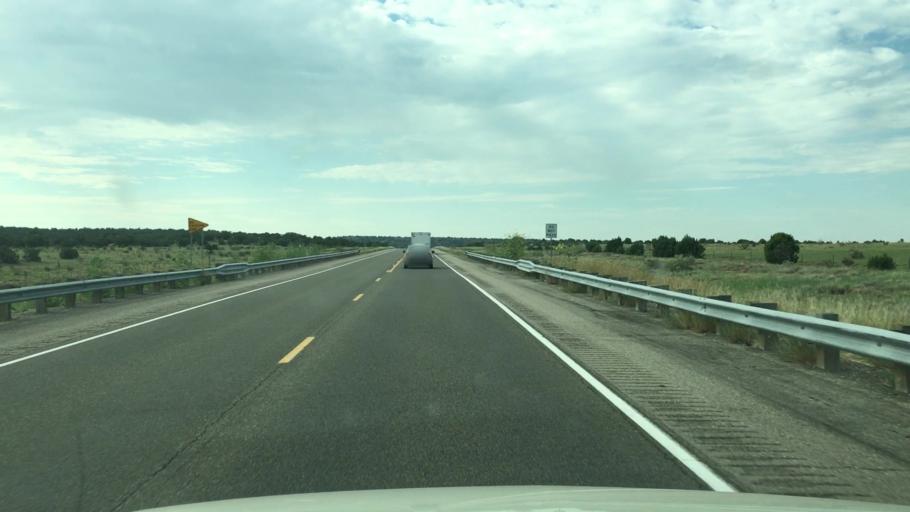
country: US
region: New Mexico
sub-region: Santa Fe County
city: Eldorado at Santa Fe
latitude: 35.2926
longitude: -105.8253
